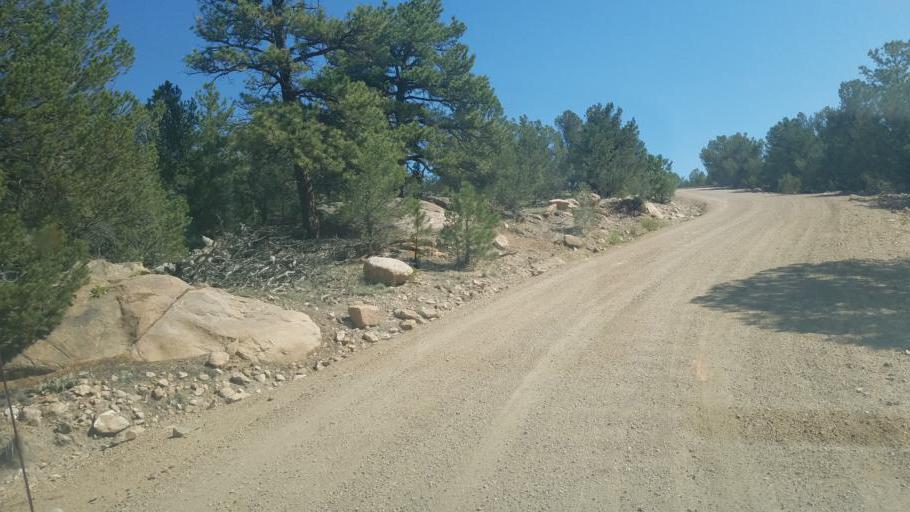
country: US
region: Colorado
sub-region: Custer County
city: Westcliffe
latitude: 38.2876
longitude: -105.4530
